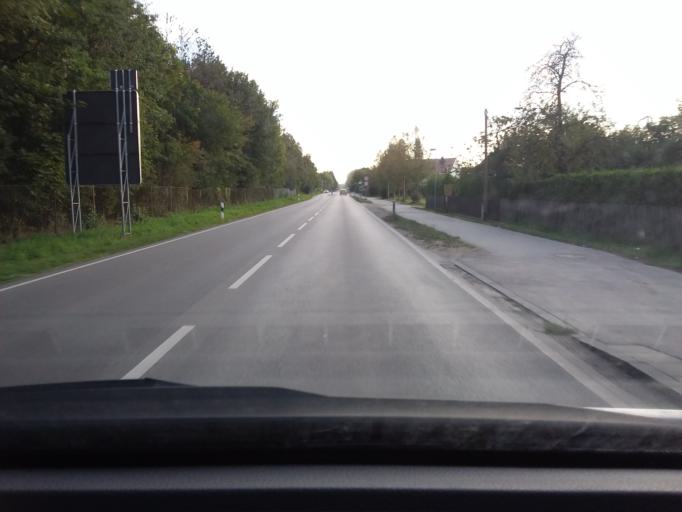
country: DE
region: Bavaria
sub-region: Upper Bavaria
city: Unterschleissheim
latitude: 48.2632
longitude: 11.5923
